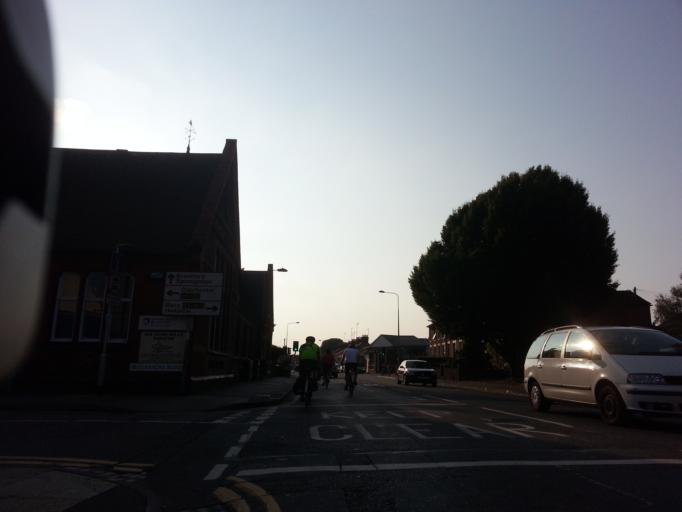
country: GB
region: England
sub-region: Suffolk
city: Ipswich
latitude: 52.0631
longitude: 1.1378
